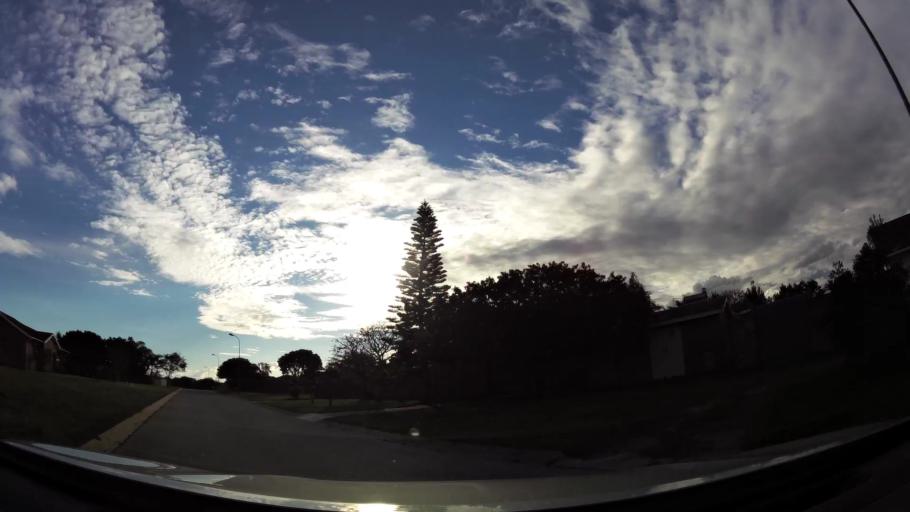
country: ZA
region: Eastern Cape
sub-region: Nelson Mandela Bay Metropolitan Municipality
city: Port Elizabeth
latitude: -33.9564
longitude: 25.4948
